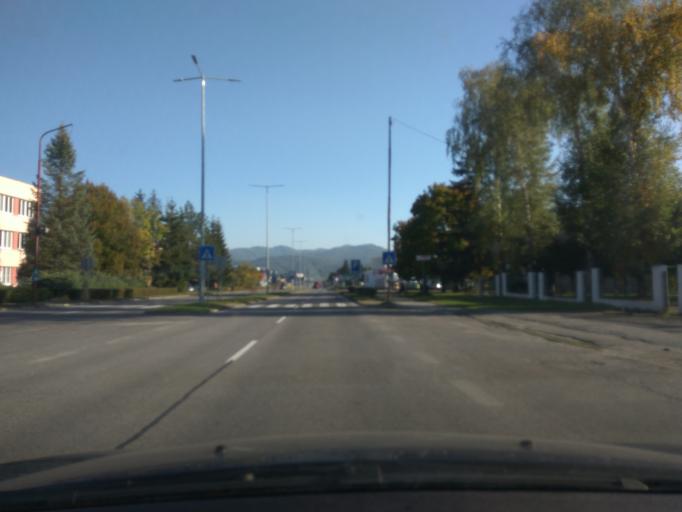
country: SK
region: Banskobystricky
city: Ziar nad Hronom
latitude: 48.5971
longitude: 18.8469
